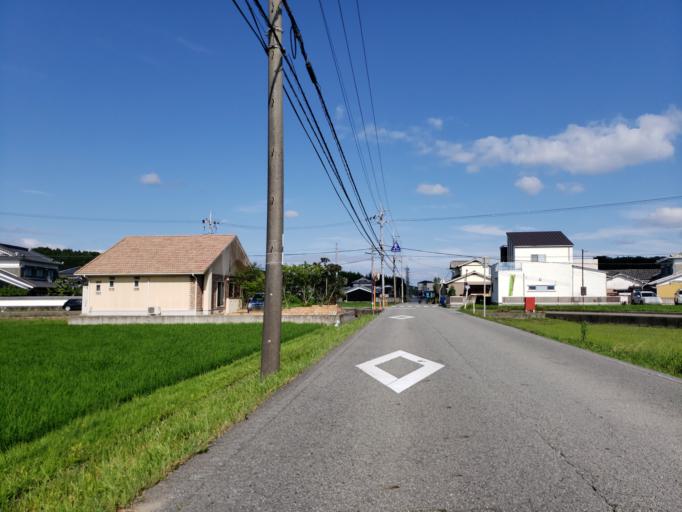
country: JP
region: Hyogo
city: Himeji
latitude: 34.9087
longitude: 134.7809
